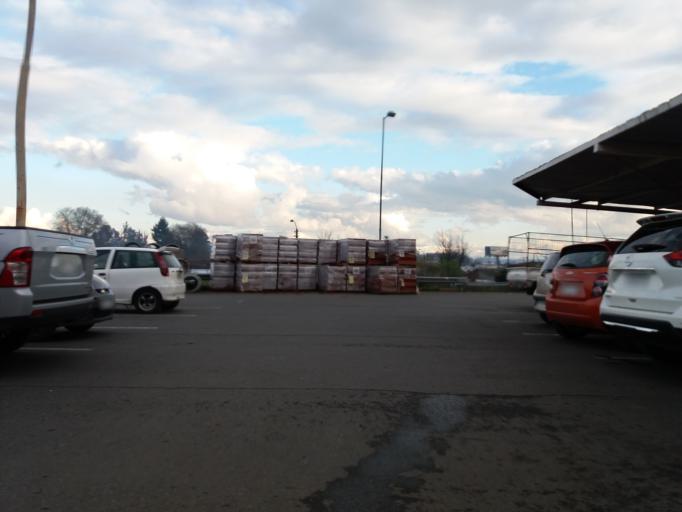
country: CL
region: Araucania
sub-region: Provincia de Cautin
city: Temuco
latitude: -38.7469
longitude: -72.6070
